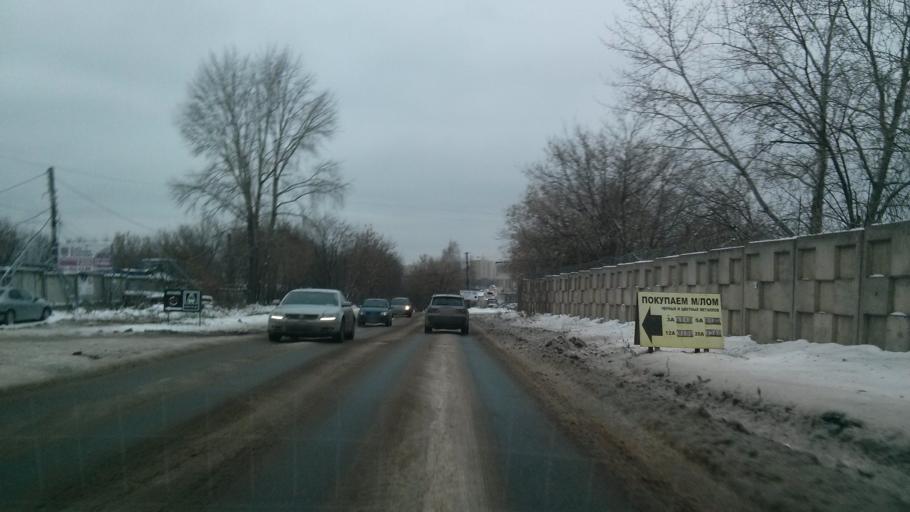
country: RU
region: Nizjnij Novgorod
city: Bor
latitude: 56.3076
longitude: 44.0553
